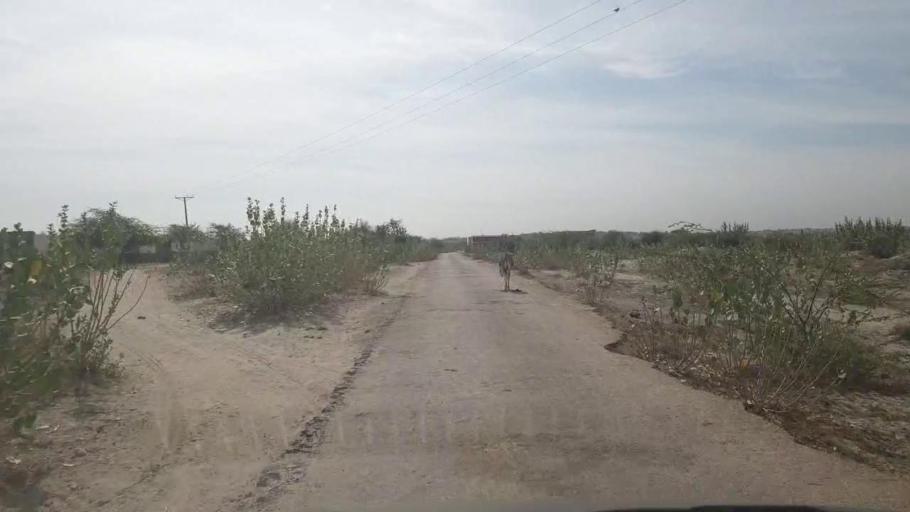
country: PK
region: Sindh
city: Umarkot
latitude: 25.2863
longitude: 69.7418
